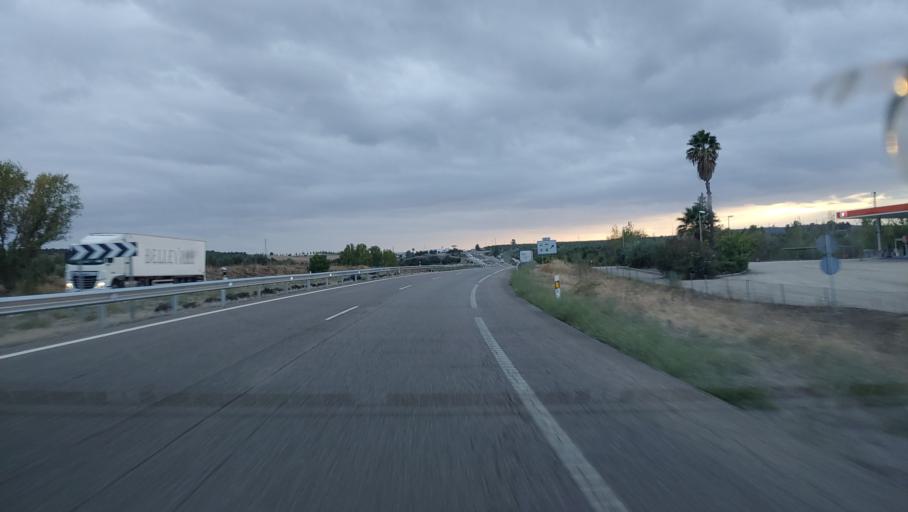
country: ES
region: Andalusia
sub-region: Provincia de Jaen
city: Guarroman
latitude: 38.1676
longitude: -3.7083
